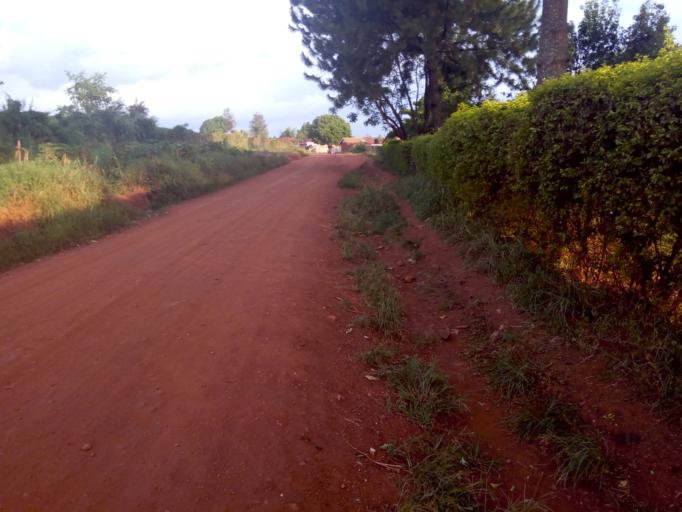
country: UG
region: Western Region
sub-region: Masindi District
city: Masindi
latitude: 1.6831
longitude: 31.7140
